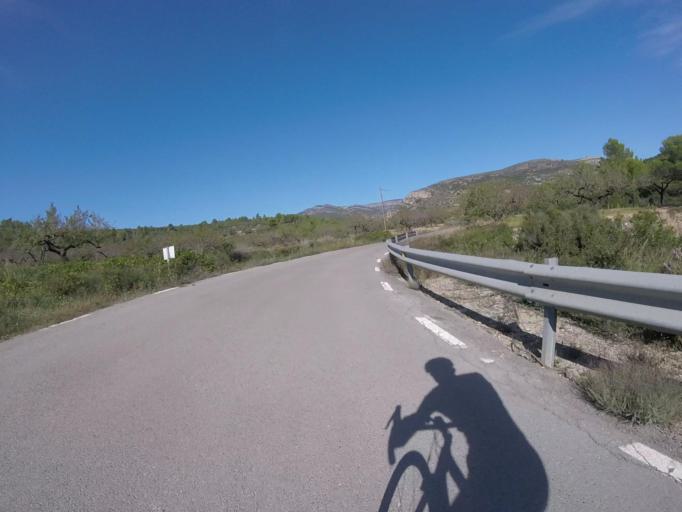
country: ES
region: Valencia
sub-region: Provincia de Castello
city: Sarratella
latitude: 40.2714
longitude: 0.0389
